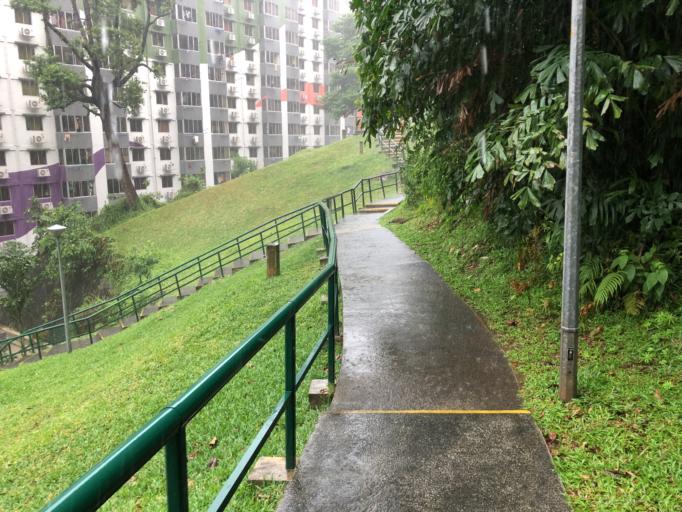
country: SG
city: Singapore
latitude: 1.2851
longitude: 103.8405
